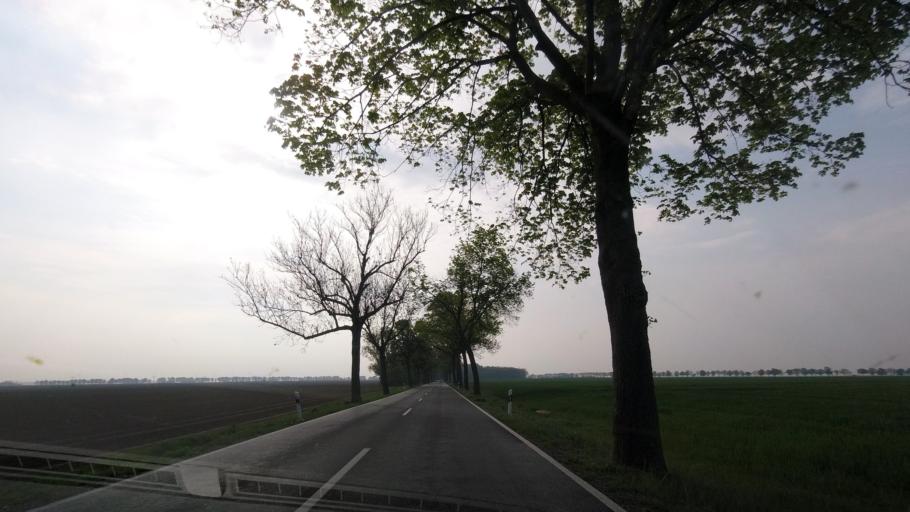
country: DE
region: Brandenburg
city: Ihlow
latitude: 51.9147
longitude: 13.2344
